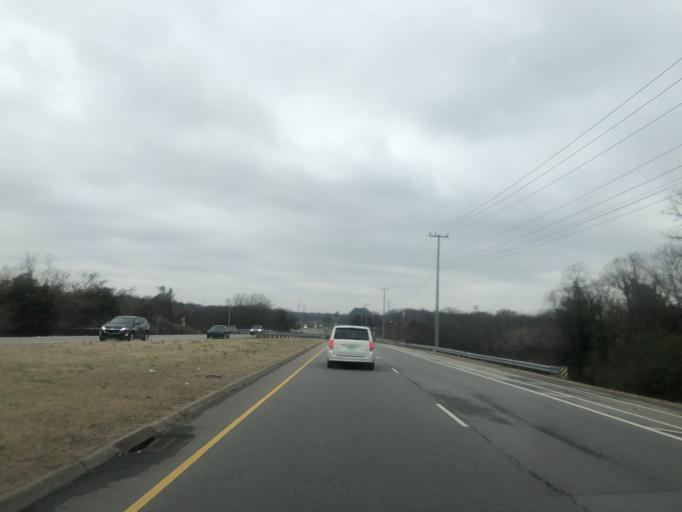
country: US
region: Tennessee
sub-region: Davidson County
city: Lakewood
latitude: 36.1552
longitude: -86.6275
